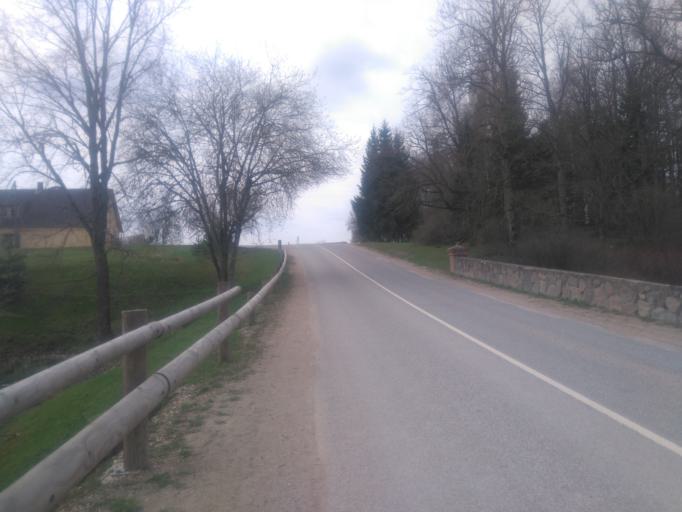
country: LV
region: Vecpiebalga
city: Vecpiebalga
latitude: 57.0181
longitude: 25.8305
